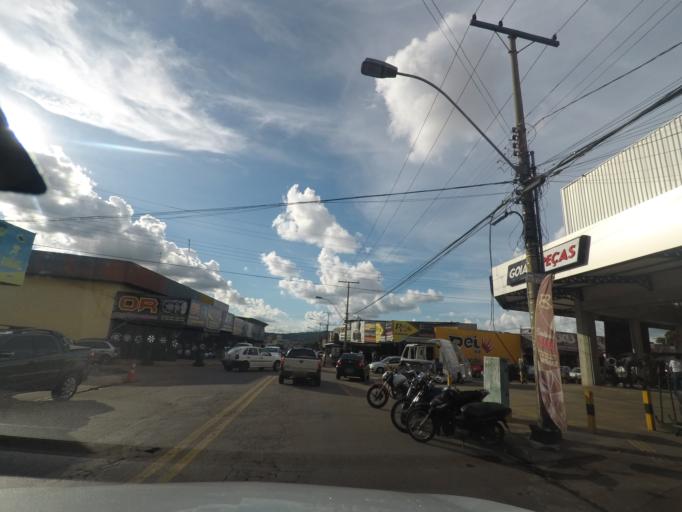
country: BR
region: Goias
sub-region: Goiania
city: Goiania
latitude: -16.6941
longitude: -49.3169
